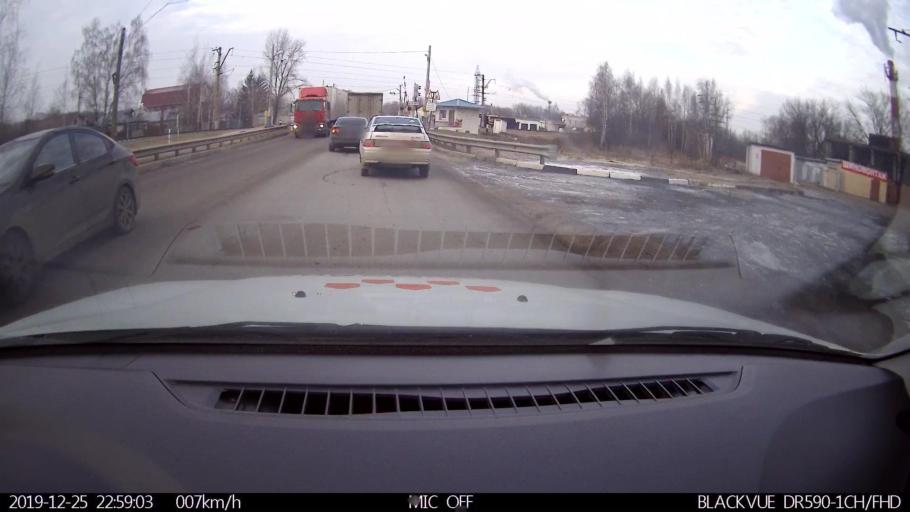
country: RU
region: Nizjnij Novgorod
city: Gorbatovka
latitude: 56.3472
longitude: 43.8381
